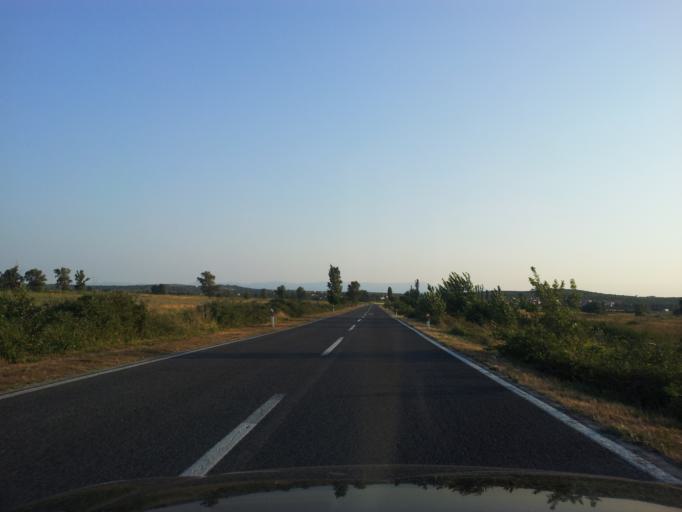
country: HR
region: Zadarska
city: Biograd na Moru
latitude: 43.9795
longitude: 15.4855
